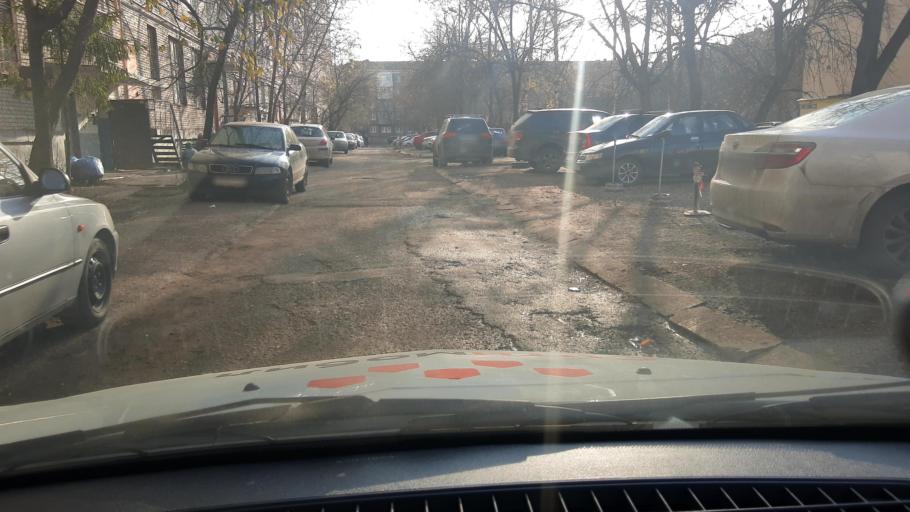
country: RU
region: Bashkortostan
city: Ufa
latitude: 54.7414
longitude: 56.0248
